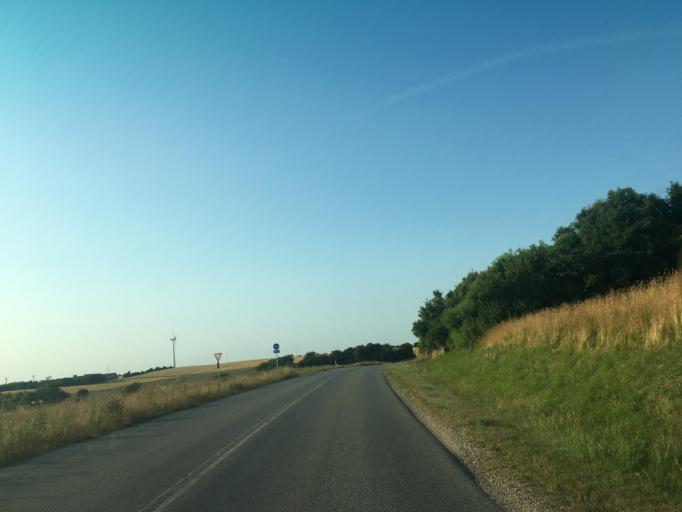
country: DK
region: North Denmark
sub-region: Thisted Kommune
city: Hurup
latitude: 56.7671
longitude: 8.4209
